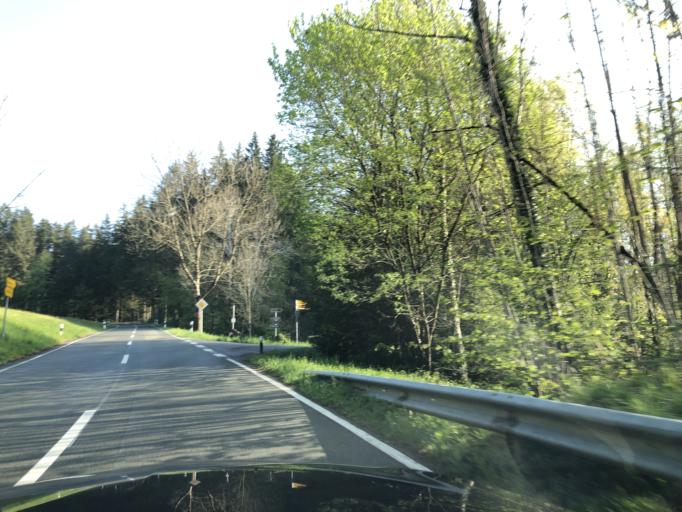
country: DE
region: Bavaria
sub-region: Upper Bavaria
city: Samerberg
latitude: 47.7984
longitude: 12.2275
